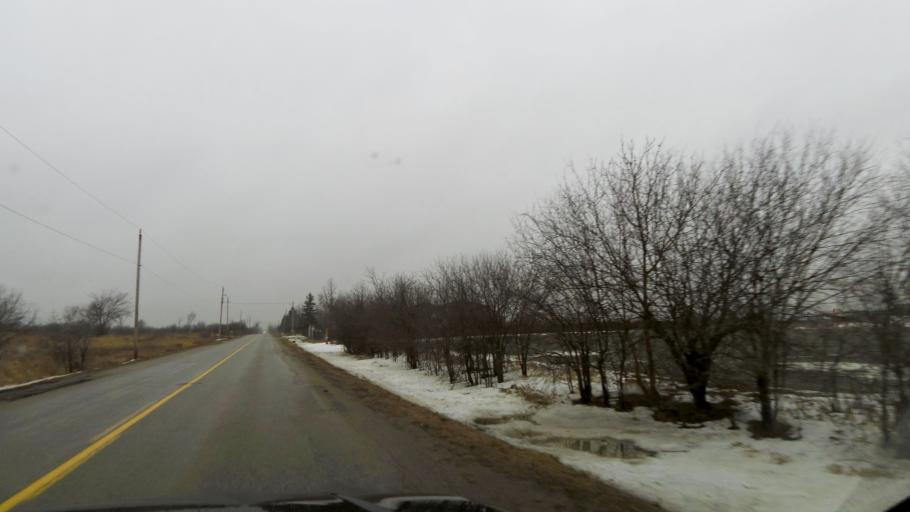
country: CA
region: Ontario
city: Brampton
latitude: 43.8118
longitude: -79.7642
